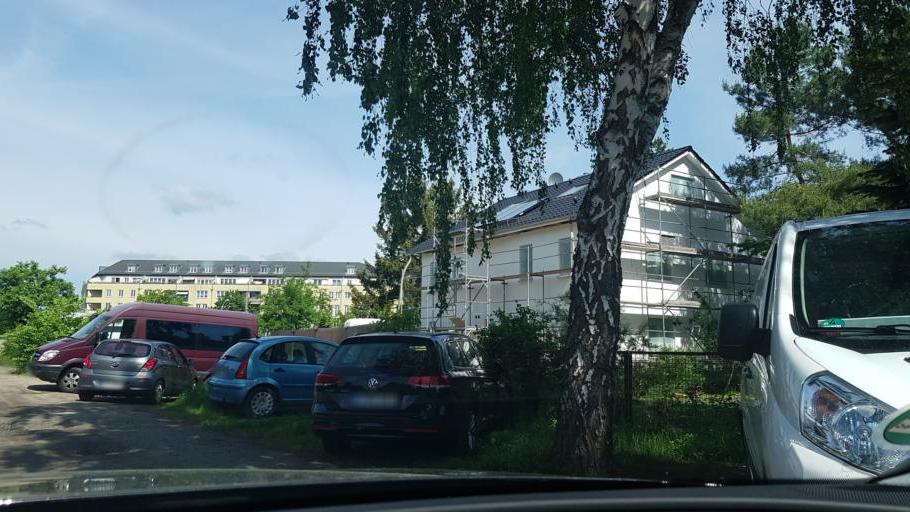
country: DE
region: Berlin
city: Buchholz
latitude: 52.6061
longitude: 13.4253
